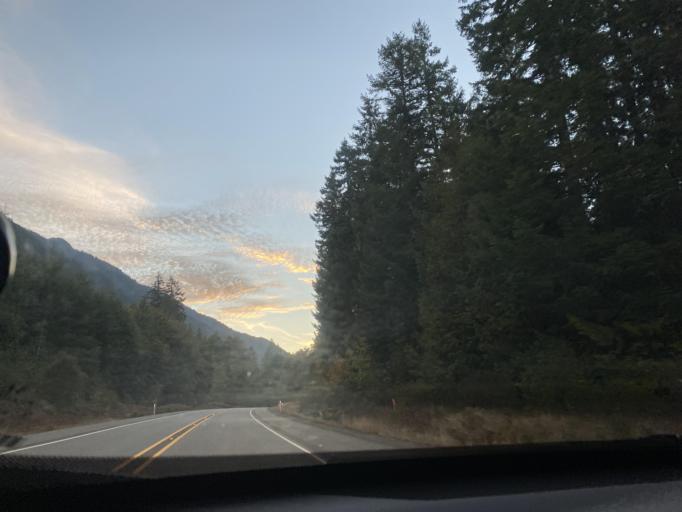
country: US
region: Washington
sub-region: Clallam County
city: Port Angeles
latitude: 48.0638
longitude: -123.5963
